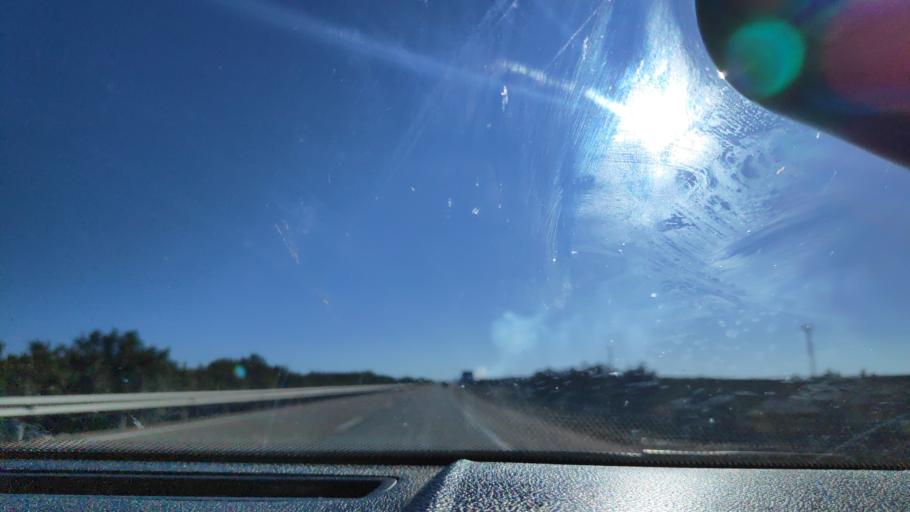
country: ES
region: Extremadura
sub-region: Provincia de Badajoz
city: Los Santos de Maimona
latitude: 38.4883
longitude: -6.3556
